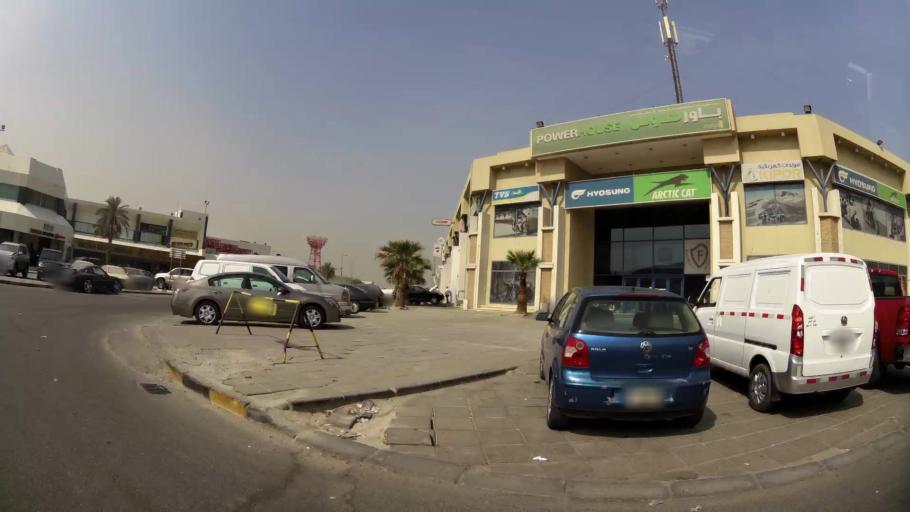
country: KW
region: Al Asimah
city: Ash Shamiyah
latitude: 29.3310
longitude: 47.9445
